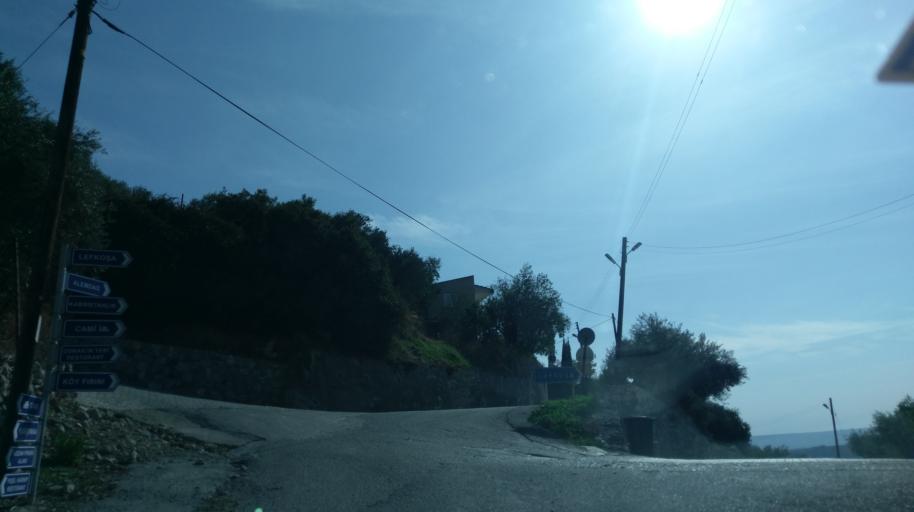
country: CY
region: Keryneia
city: Lapithos
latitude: 35.3128
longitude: 33.1394
